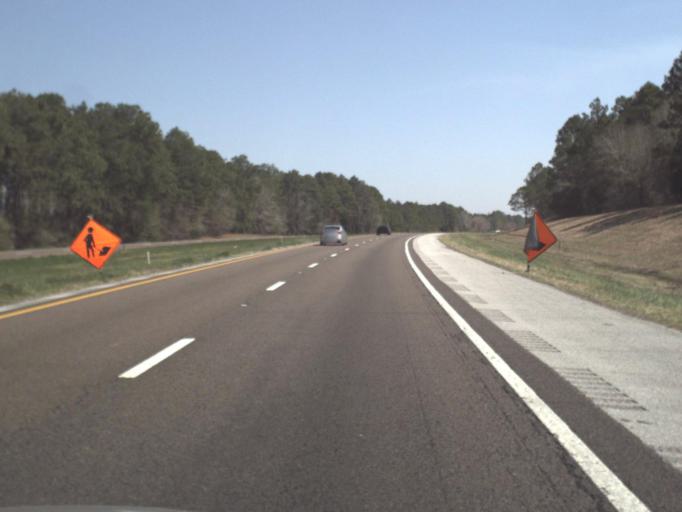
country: US
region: Florida
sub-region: Holmes County
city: Bonifay
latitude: 30.7618
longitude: -85.6576
